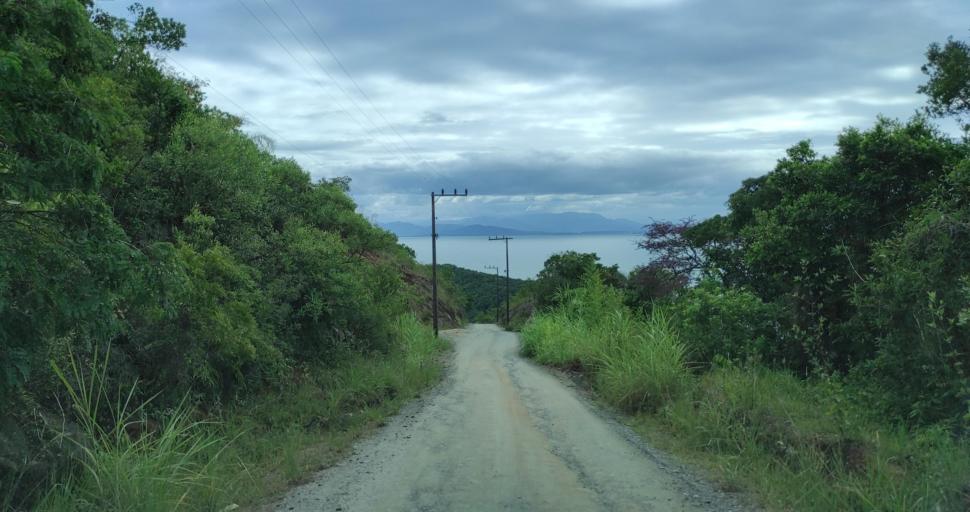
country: BR
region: Santa Catarina
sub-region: Porto Belo
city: Porto Belo
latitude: -27.2128
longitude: -48.5052
